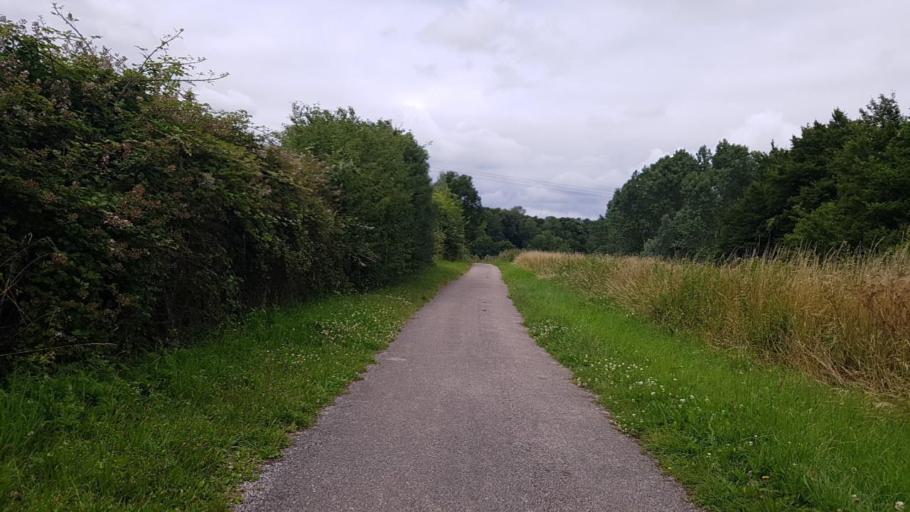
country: FR
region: Picardie
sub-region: Departement de l'Aisne
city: La Capelle
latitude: 49.9075
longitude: 3.9177
